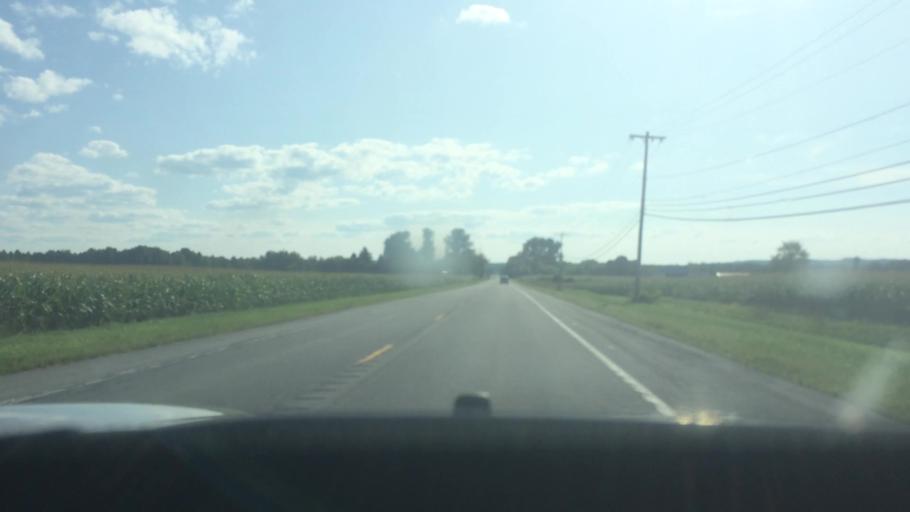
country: US
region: New York
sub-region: Franklin County
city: Malone
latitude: 44.8377
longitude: -74.3165
